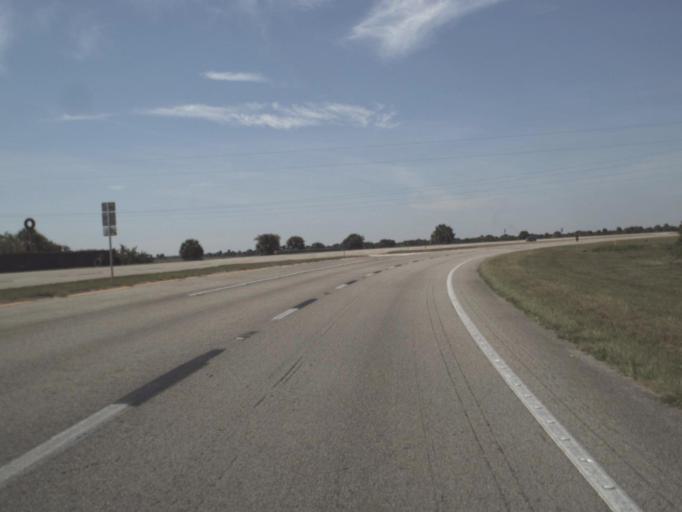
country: US
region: Florida
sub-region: Glades County
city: Moore Haven
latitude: 26.8339
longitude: -81.1888
